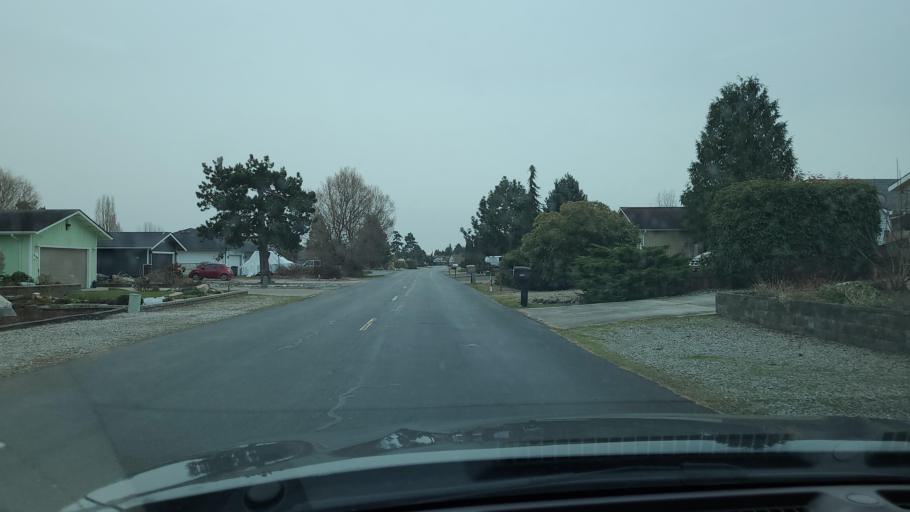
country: US
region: Washington
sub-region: Whatcom County
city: Birch Bay
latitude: 48.9404
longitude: -122.7841
